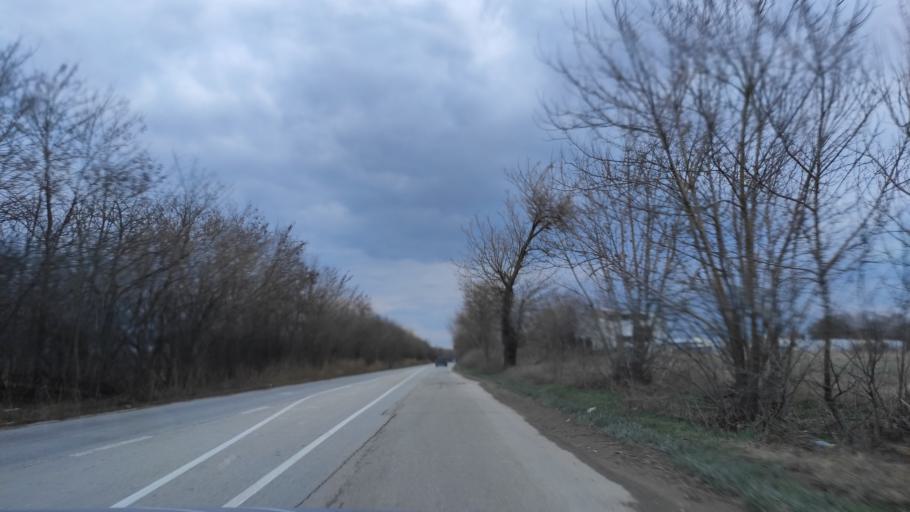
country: BG
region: Varna
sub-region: Obshtina Aksakovo
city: Aksakovo
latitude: 43.2281
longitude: 27.8449
